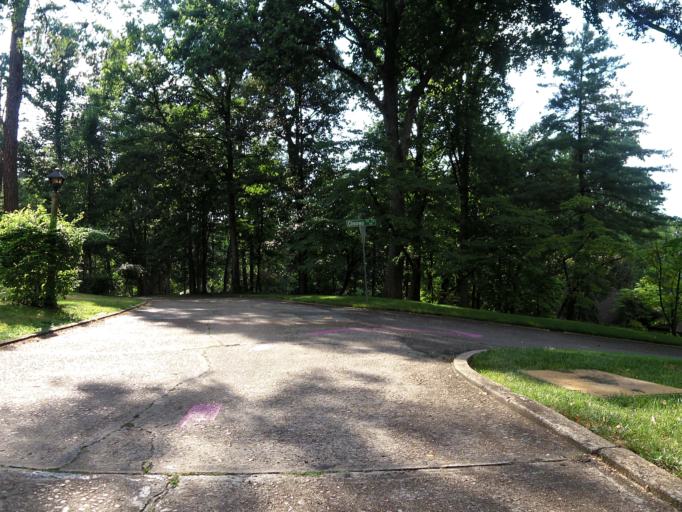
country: US
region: Tennessee
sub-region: Knox County
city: Knoxville
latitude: 35.9416
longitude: -83.9589
